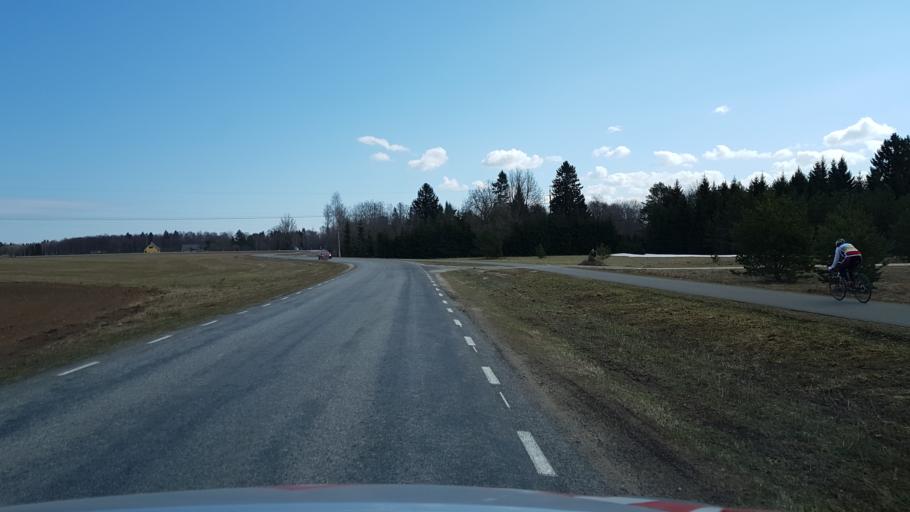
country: EE
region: Laeaene-Virumaa
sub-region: Rakvere linn
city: Rakvere
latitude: 59.3828
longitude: 26.3115
